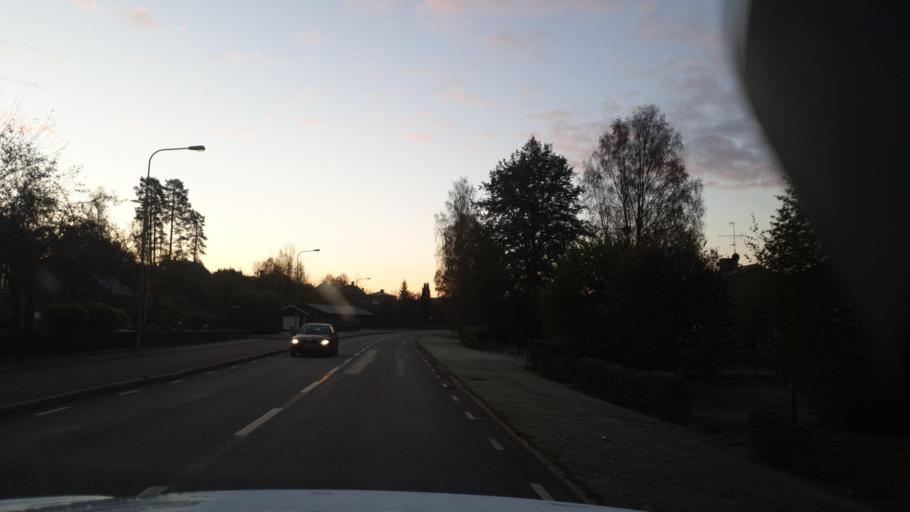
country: SE
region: Vaermland
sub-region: Eda Kommun
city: Amotfors
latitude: 59.7658
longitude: 12.3587
